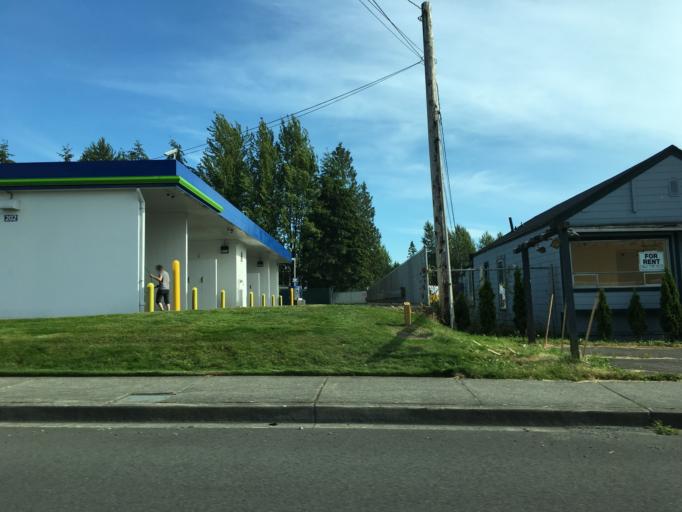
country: US
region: Washington
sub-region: Snohomish County
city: Martha Lake
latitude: 47.8494
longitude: -122.2375
